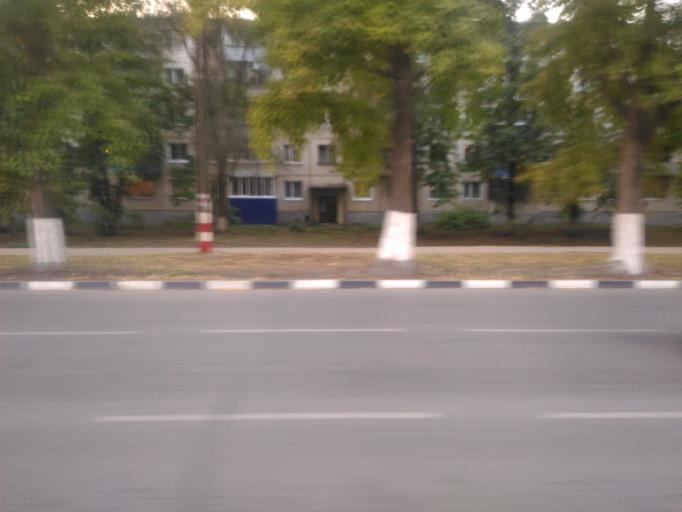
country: RU
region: Ulyanovsk
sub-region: Ulyanovskiy Rayon
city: Ulyanovsk
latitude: 54.2711
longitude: 48.2865
